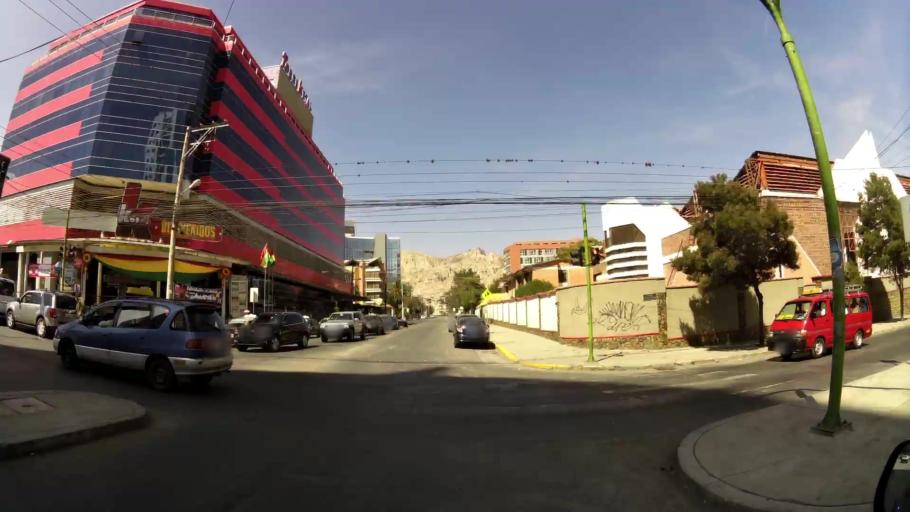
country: BO
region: La Paz
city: La Paz
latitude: -16.5392
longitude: -68.0843
